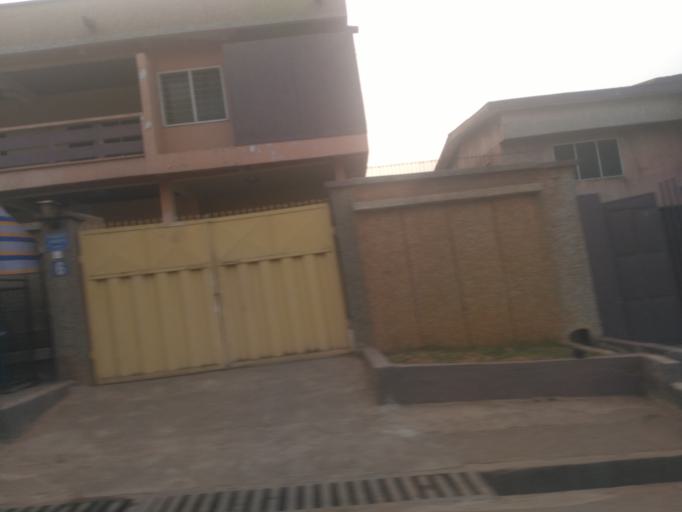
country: GH
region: Ashanti
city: Kumasi
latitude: 6.6700
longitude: -1.6032
